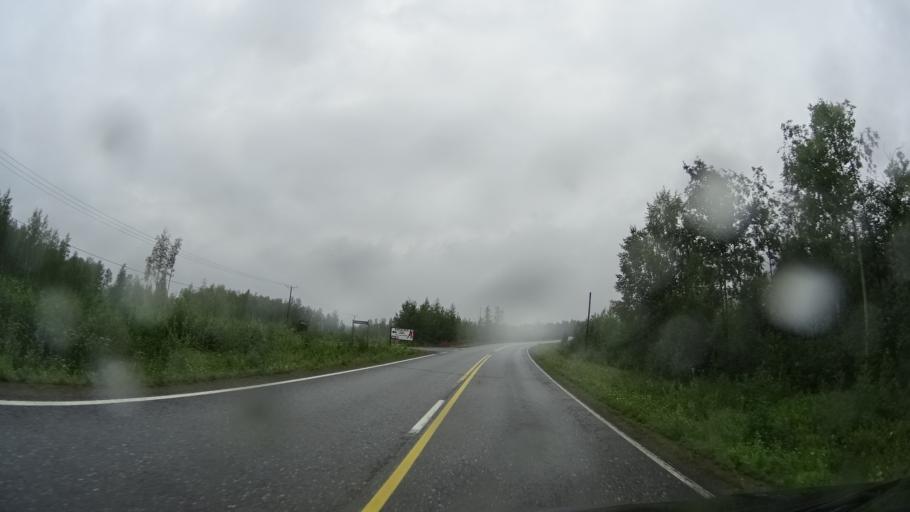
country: FI
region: North Karelia
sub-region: Keski-Karjala
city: Raeaekkylae
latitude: 62.3111
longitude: 29.5200
